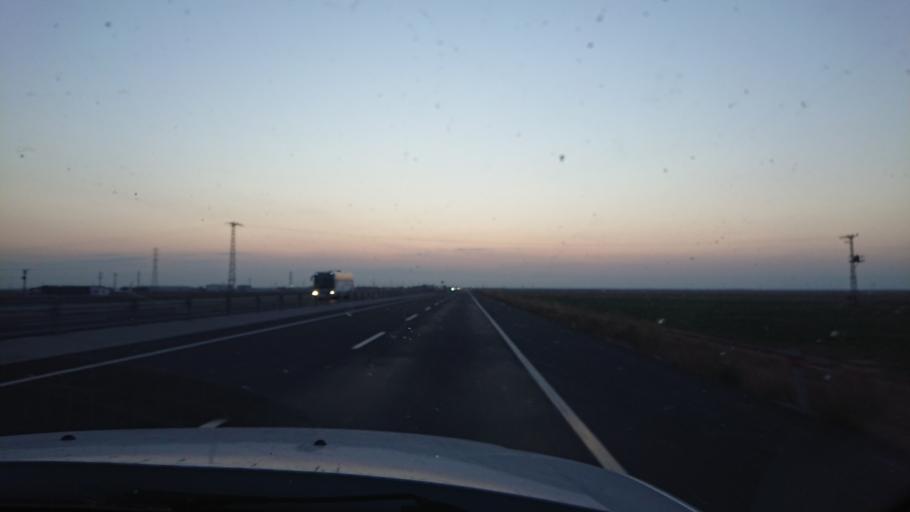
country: TR
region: Aksaray
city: Yesilova
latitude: 38.3068
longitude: 33.8179
